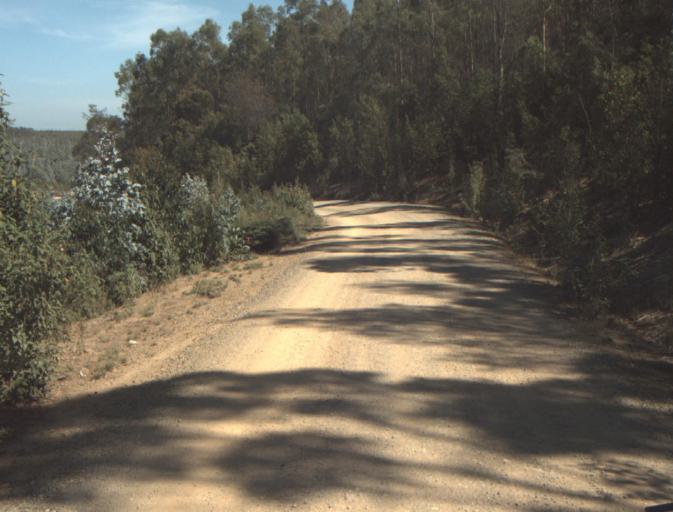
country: AU
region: Tasmania
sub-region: Launceston
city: Mayfield
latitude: -41.2236
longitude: 147.2477
